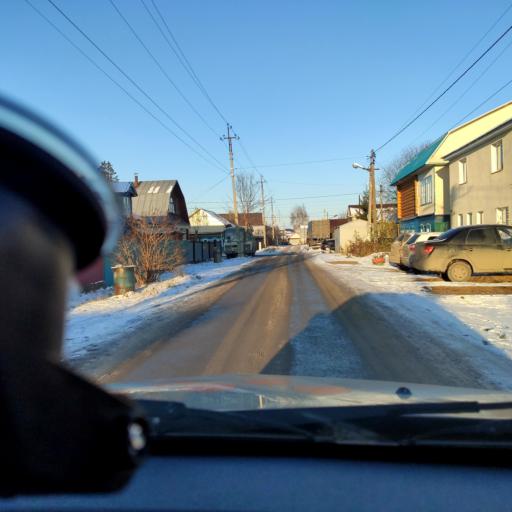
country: RU
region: Bashkortostan
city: Ufa
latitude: 54.7407
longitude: 55.9154
